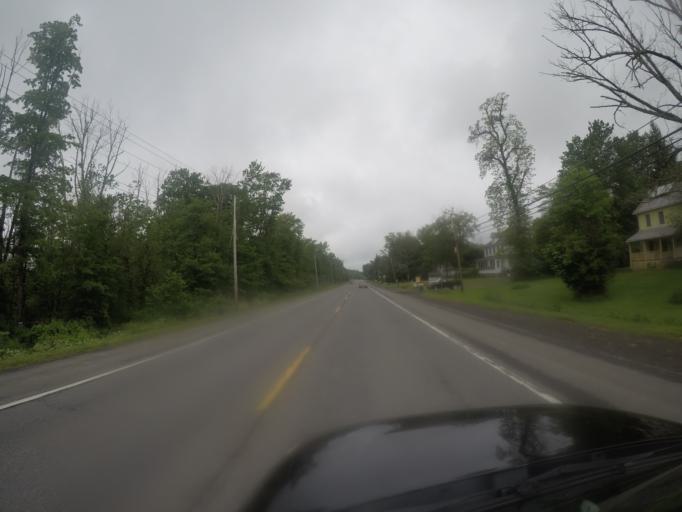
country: US
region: New York
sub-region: Ulster County
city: Shokan
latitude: 41.9769
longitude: -74.1932
